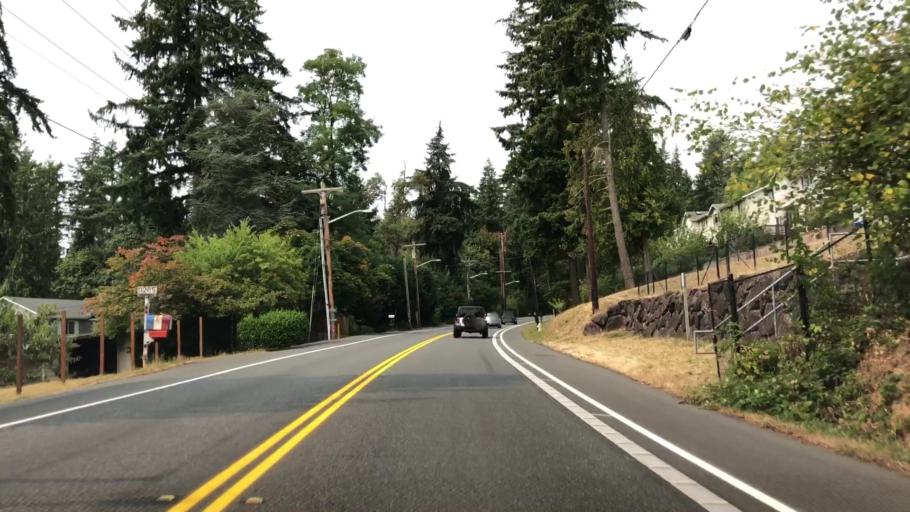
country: US
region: Washington
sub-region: King County
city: Inglewood-Finn Hill
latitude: 47.7026
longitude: -122.2365
